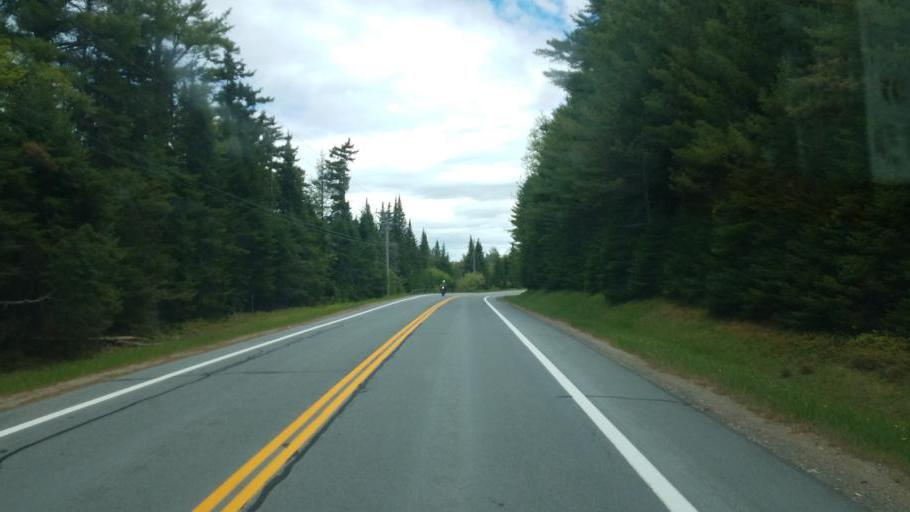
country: US
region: New York
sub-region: Hamilton County
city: Lake Pleasant
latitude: 43.8337
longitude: -74.5605
